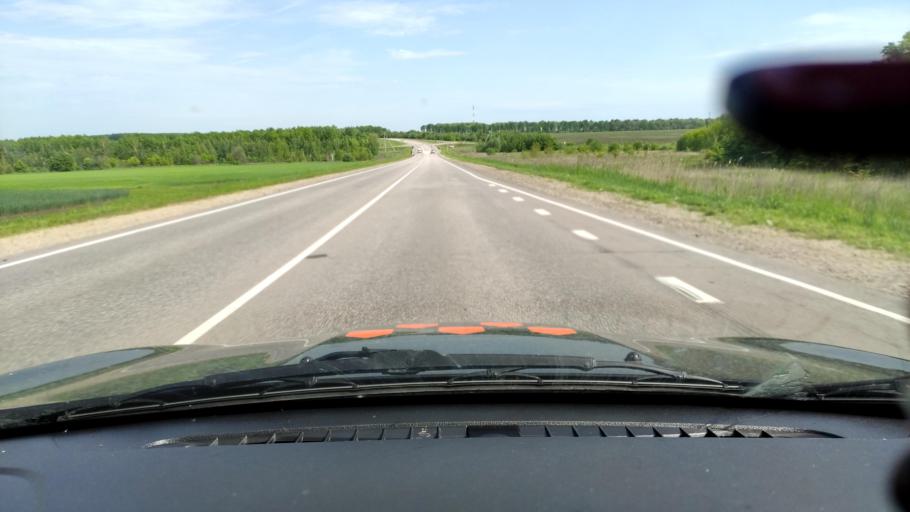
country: RU
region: Voronezj
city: Kolodeznyy
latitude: 51.3648
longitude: 39.0235
